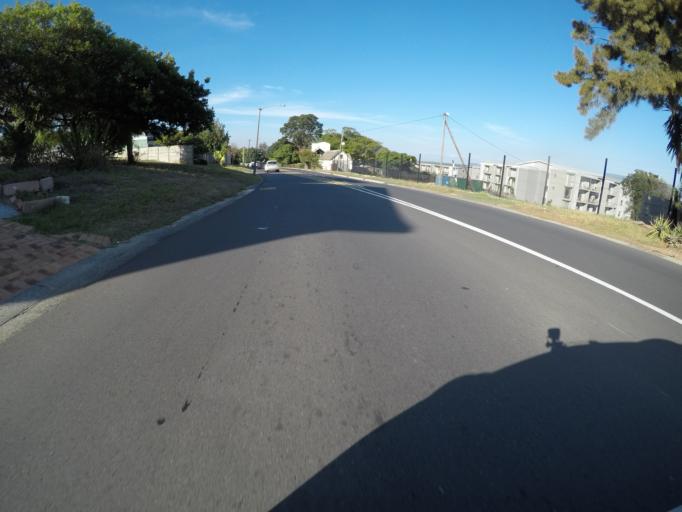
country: ZA
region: Western Cape
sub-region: City of Cape Town
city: Kraaifontein
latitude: -33.8733
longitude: 18.6479
